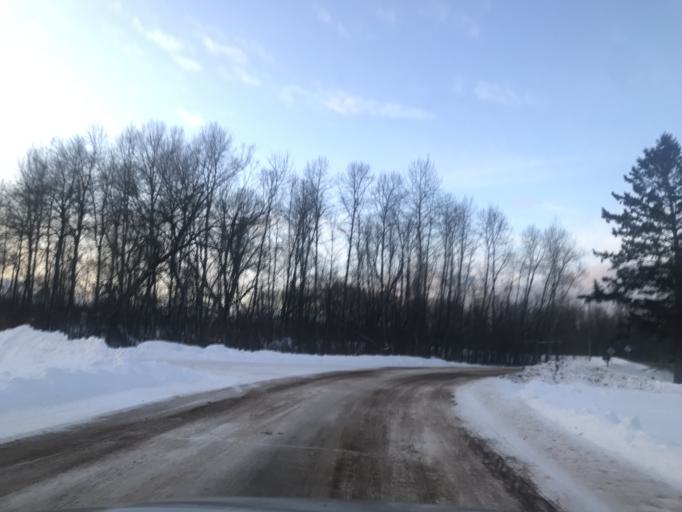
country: US
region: Michigan
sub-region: Menominee County
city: Menominee
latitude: 45.4139
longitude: -87.3483
